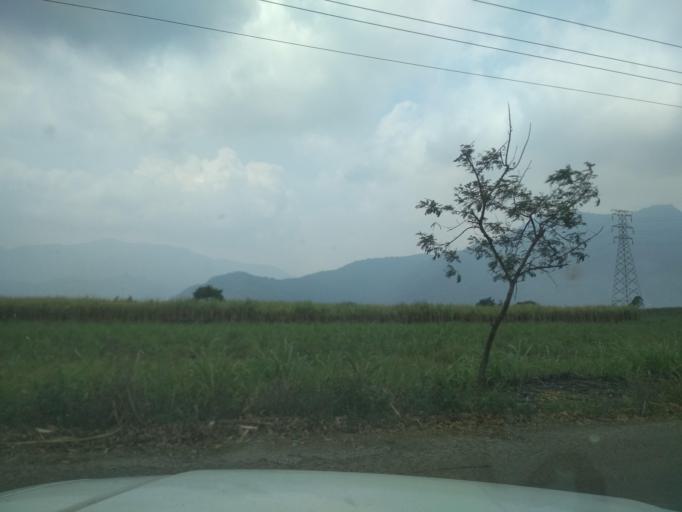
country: MX
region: Veracruz
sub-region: Cordoba
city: San Jose de Tapia
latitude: 18.8364
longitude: -96.9774
